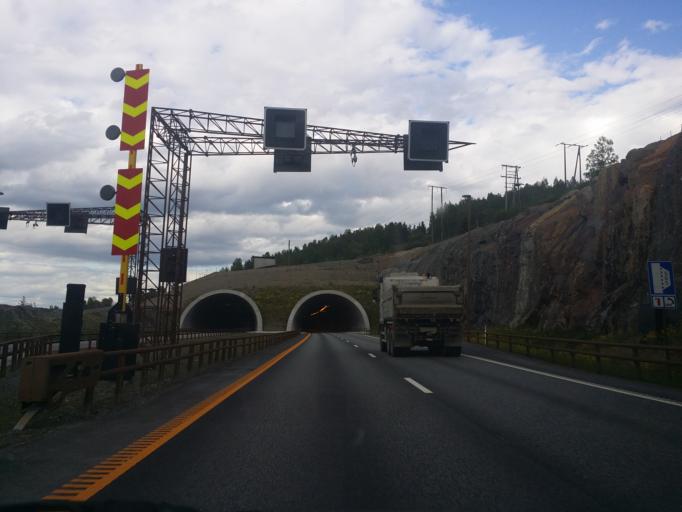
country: NO
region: Hedmark
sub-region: Stange
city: Stange
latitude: 60.5736
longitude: 11.2675
